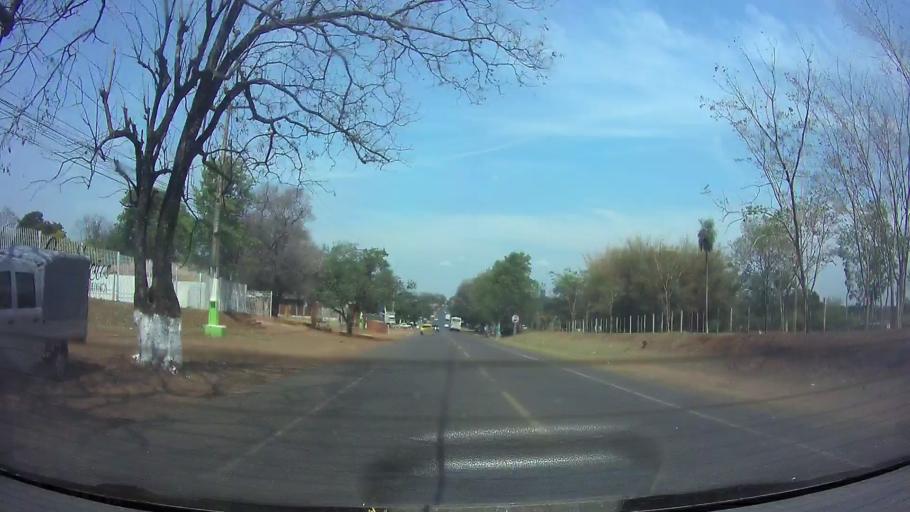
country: PY
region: Central
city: Guarambare
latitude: -25.4391
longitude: -57.4443
